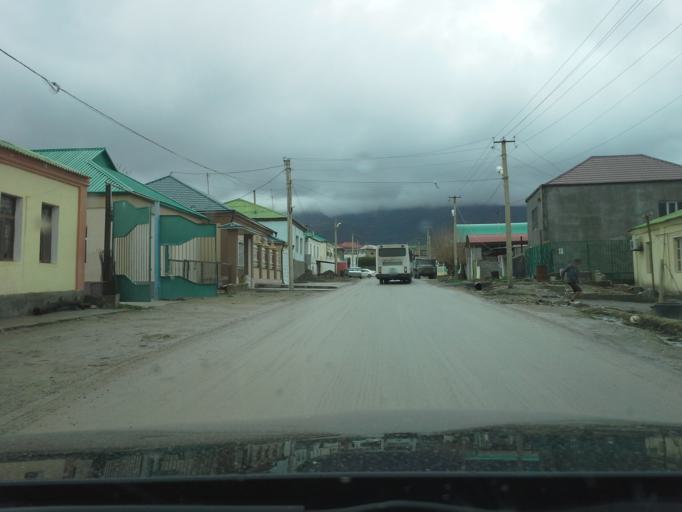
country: TM
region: Ahal
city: Abadan
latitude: 37.9612
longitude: 58.2145
